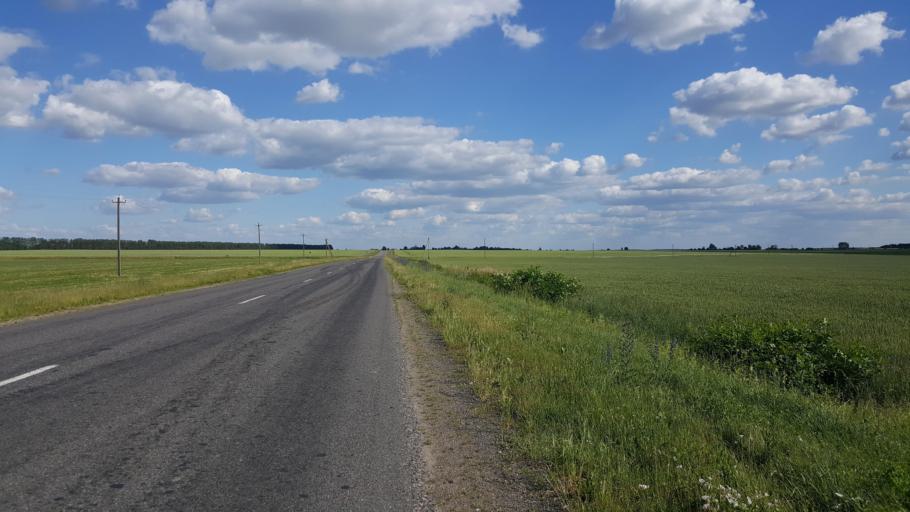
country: BY
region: Brest
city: Kamyanyets
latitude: 52.4627
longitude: 23.7193
